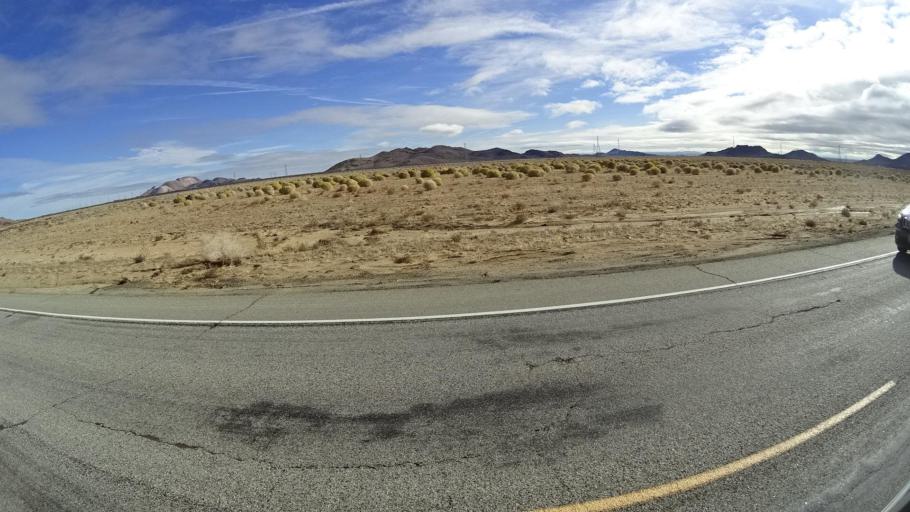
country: US
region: California
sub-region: Kern County
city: Rosamond
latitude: 34.9186
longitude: -118.2915
